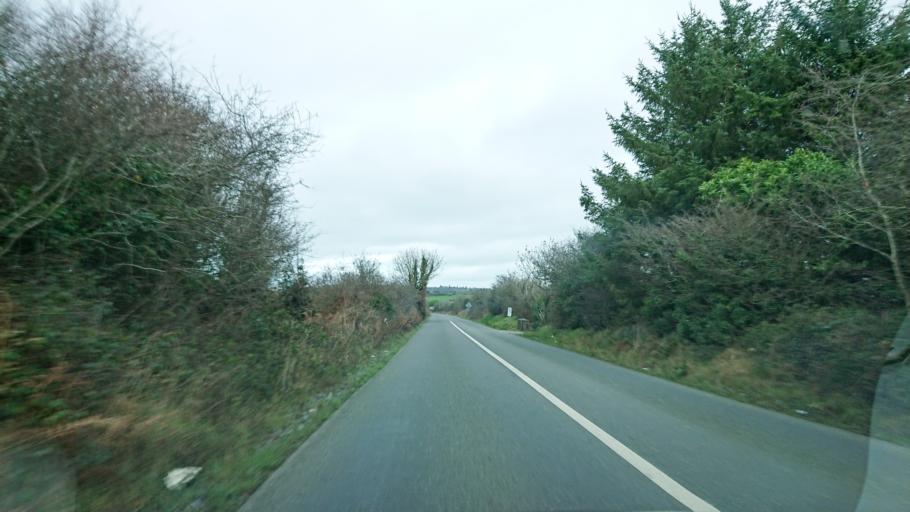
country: IE
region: Leinster
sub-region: Kilkenny
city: Mooncoin
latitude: 52.2145
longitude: -7.2413
